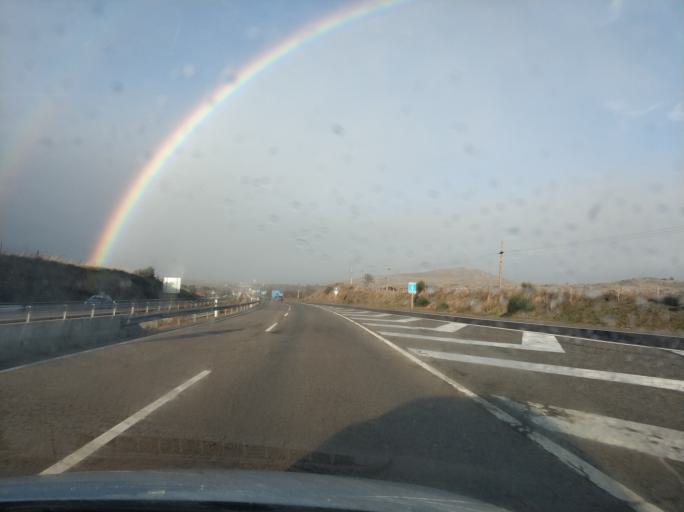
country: ES
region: Madrid
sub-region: Provincia de Madrid
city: Gascones
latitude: 41.0131
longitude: -3.6305
